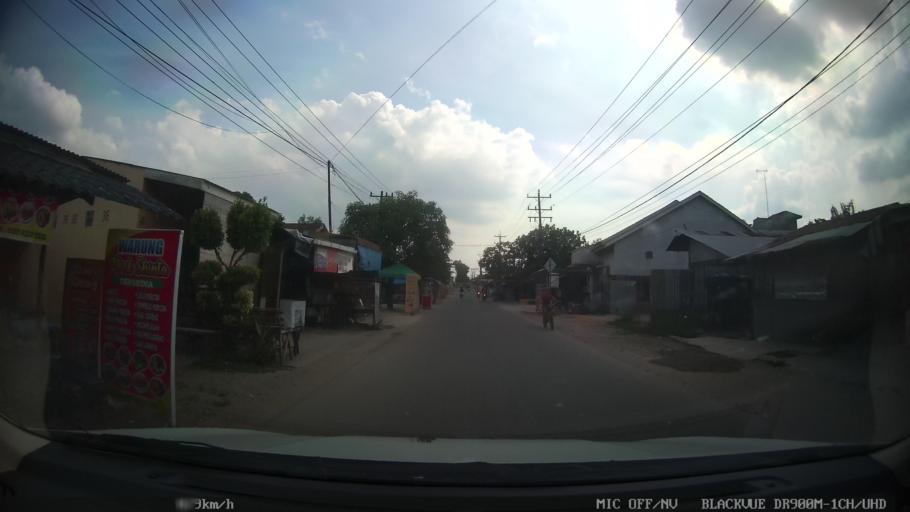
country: ID
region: North Sumatra
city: Binjai
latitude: 3.6371
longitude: 98.4917
